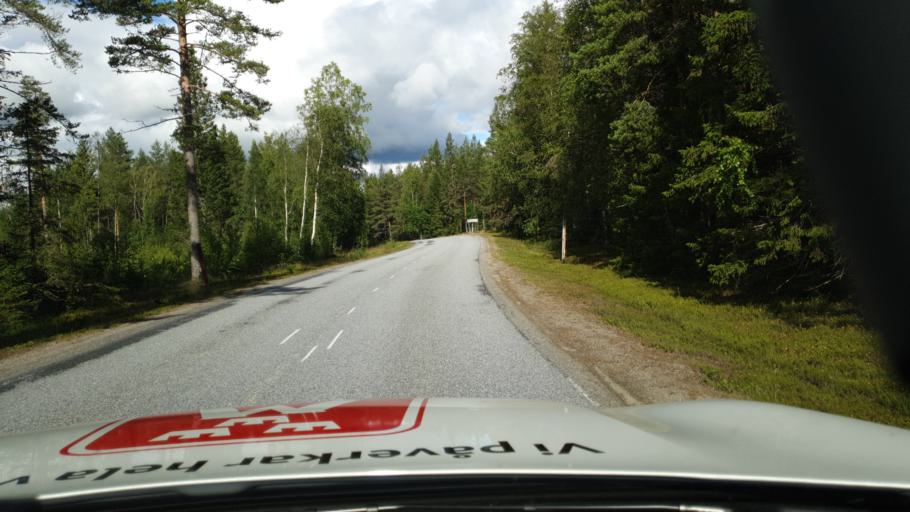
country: SE
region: Vaesterbotten
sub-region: Umea Kommun
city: Roback
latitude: 63.6769
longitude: 20.0819
